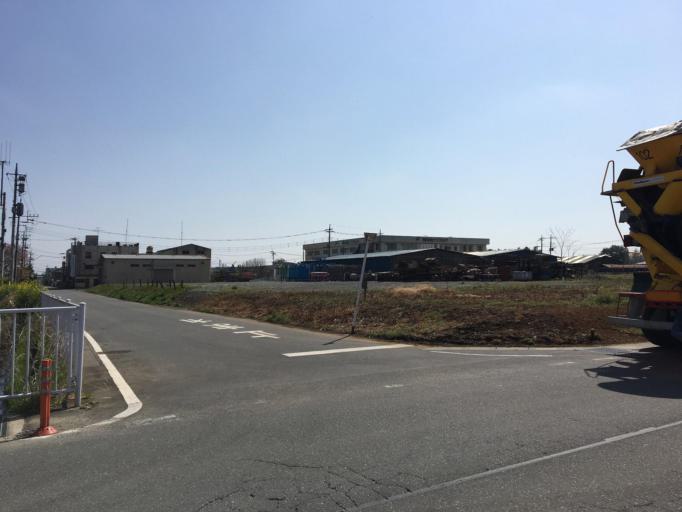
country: JP
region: Saitama
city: Sakado
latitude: 35.9181
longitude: 139.3618
